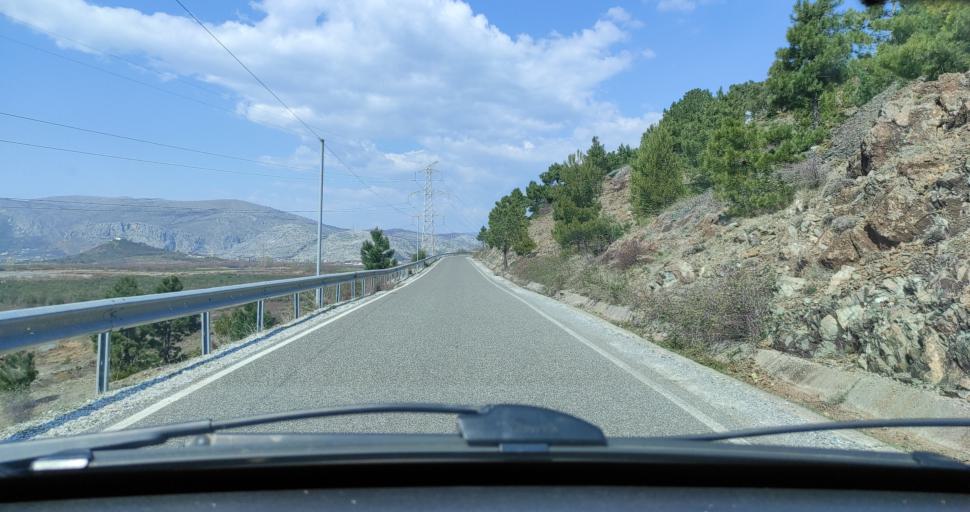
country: AL
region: Shkoder
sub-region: Rrethi i Shkodres
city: Vau i Dejes
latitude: 41.9857
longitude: 19.6436
